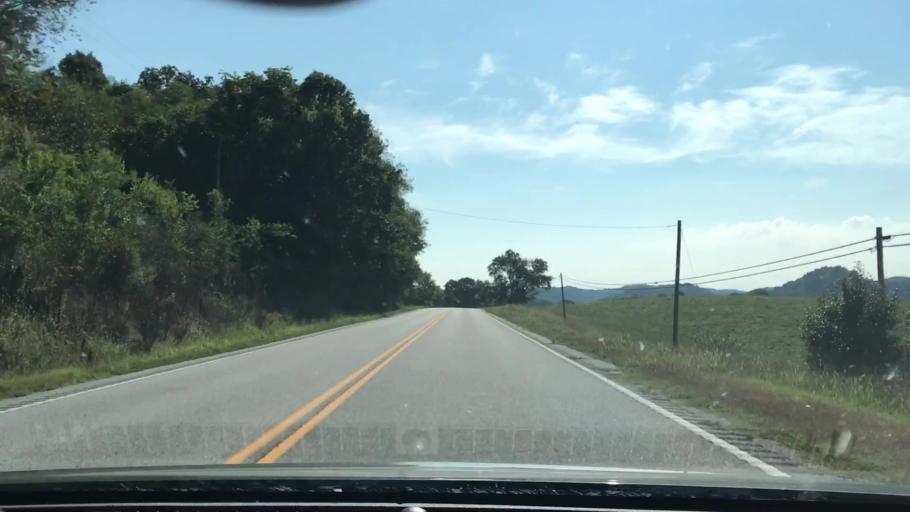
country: US
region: Tennessee
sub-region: Jackson County
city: Gainesboro
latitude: 36.3567
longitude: -85.7291
